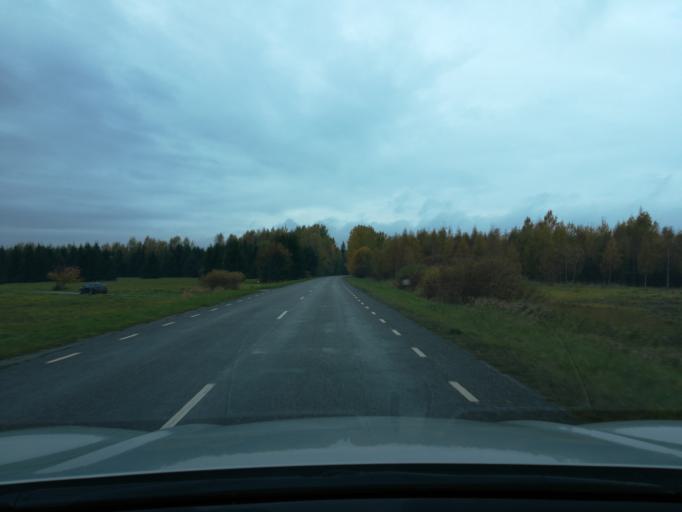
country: EE
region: Ida-Virumaa
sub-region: Johvi vald
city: Johvi
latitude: 59.0747
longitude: 27.3514
